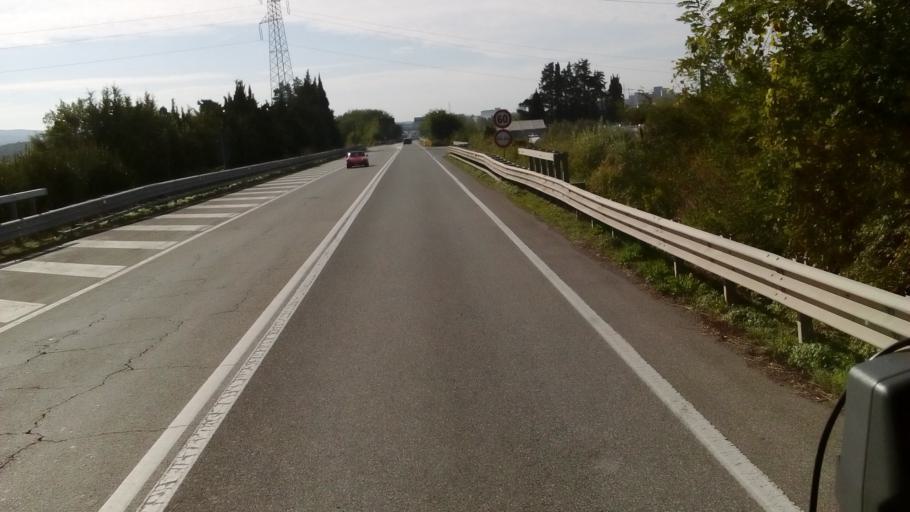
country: IT
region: Tuscany
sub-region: Provincia di Livorno
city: Livorno
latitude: 43.5818
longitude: 10.3495
